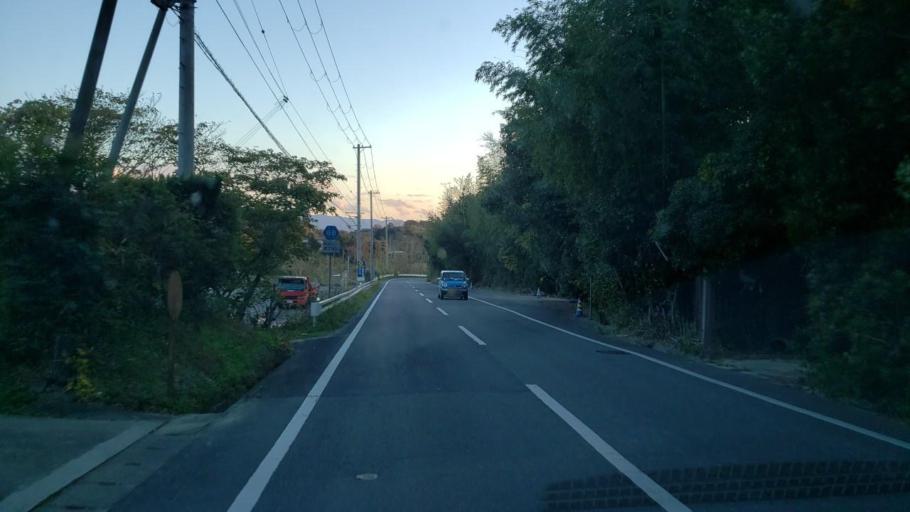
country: JP
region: Hyogo
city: Fukura
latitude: 34.3446
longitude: 134.7825
